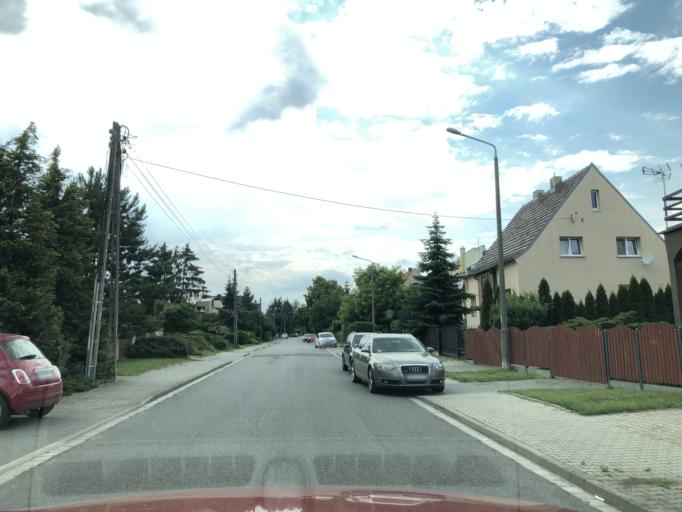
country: PL
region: Lower Silesian Voivodeship
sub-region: Powiat wroclawski
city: Smolec
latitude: 51.1543
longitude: 16.9118
